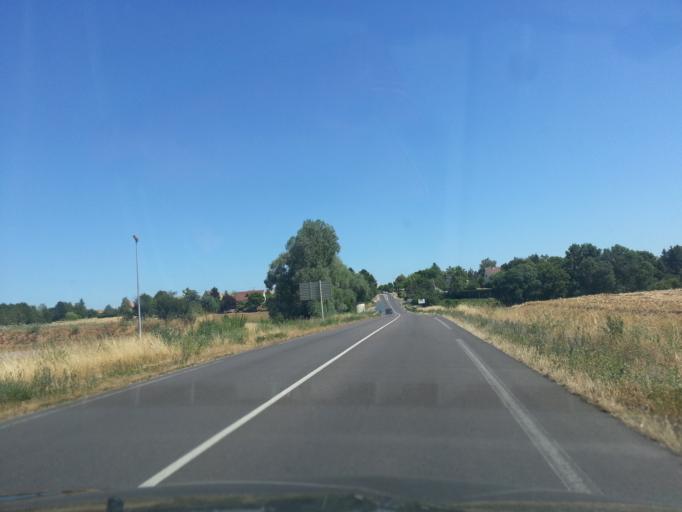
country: FR
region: Bourgogne
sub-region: Departement de Saone-et-Loire
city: Chatenoy-le-Royal
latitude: 46.7798
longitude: 4.7991
